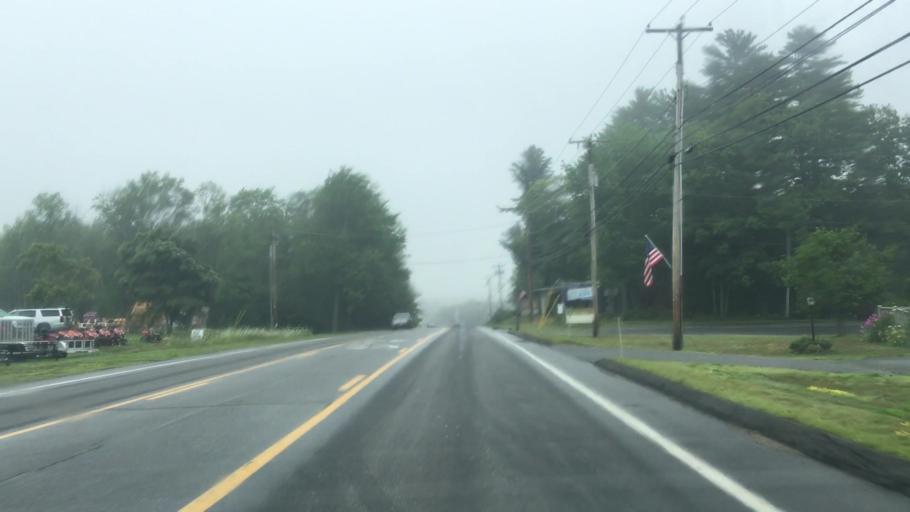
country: US
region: Maine
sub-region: Lincoln County
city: Wiscasset
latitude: 43.9858
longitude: -69.6958
